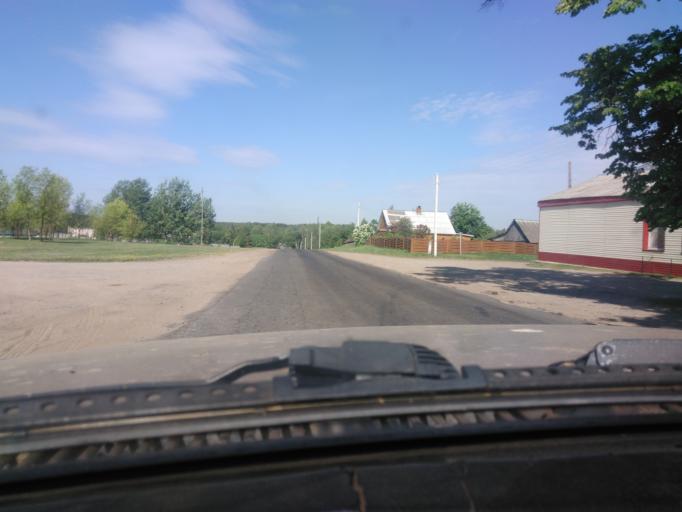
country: BY
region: Mogilev
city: Myazhysyatki
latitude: 53.8114
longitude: 30.1320
